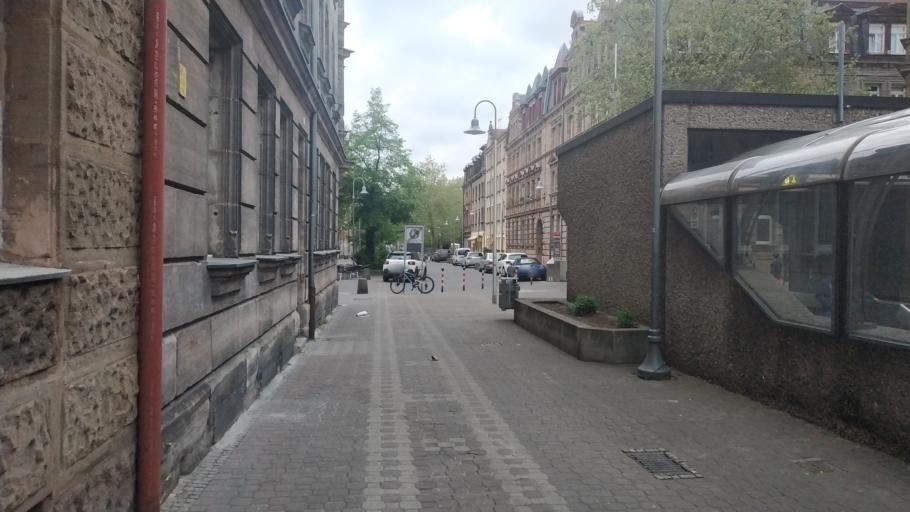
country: DE
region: Bavaria
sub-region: Regierungsbezirk Mittelfranken
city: Grossreuth bei Schweinau
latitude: 49.4392
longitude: 11.0500
